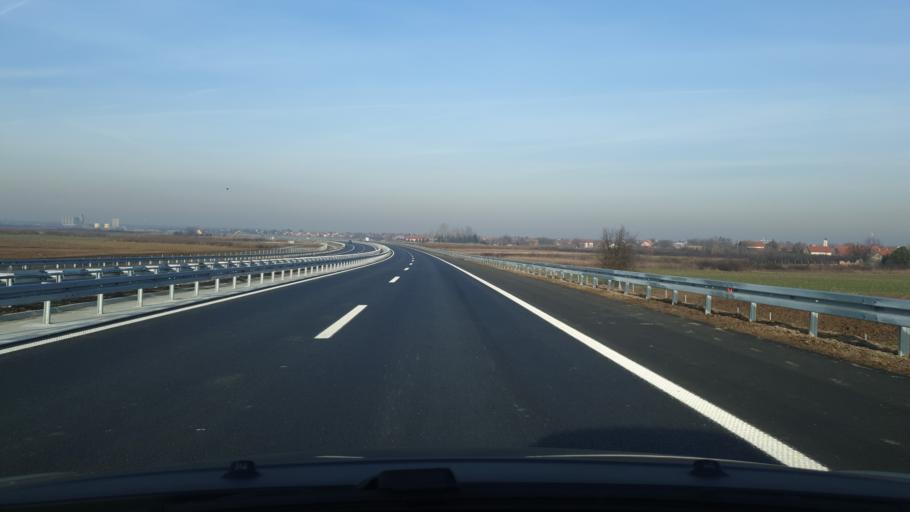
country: RS
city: Boljevci
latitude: 44.7456
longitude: 20.2496
